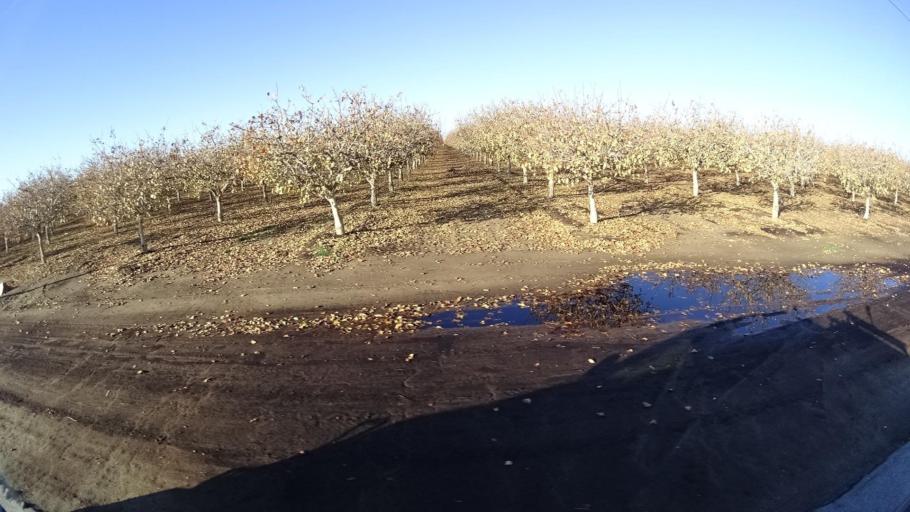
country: US
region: California
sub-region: Kern County
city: Delano
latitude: 35.7705
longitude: -119.3298
